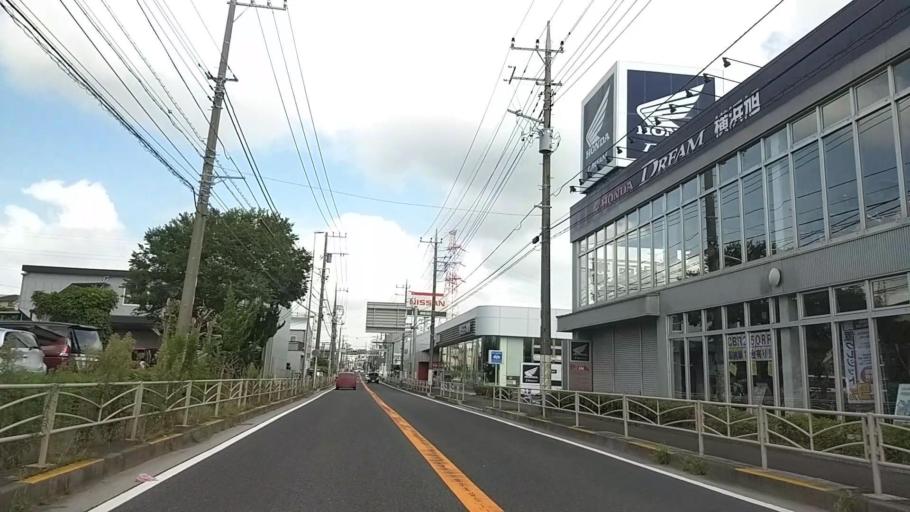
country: JP
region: Kanagawa
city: Minami-rinkan
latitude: 35.4875
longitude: 139.5193
